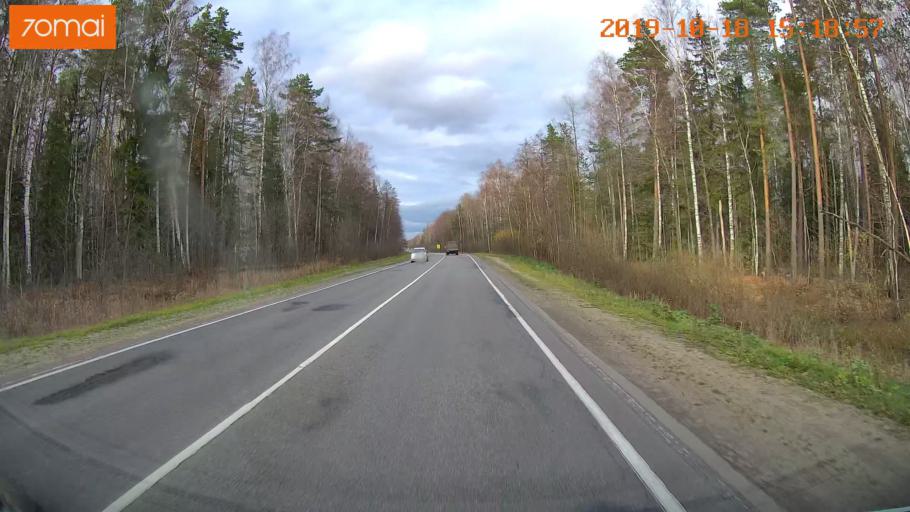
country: RU
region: Vladimir
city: Anopino
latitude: 55.6660
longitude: 40.7339
